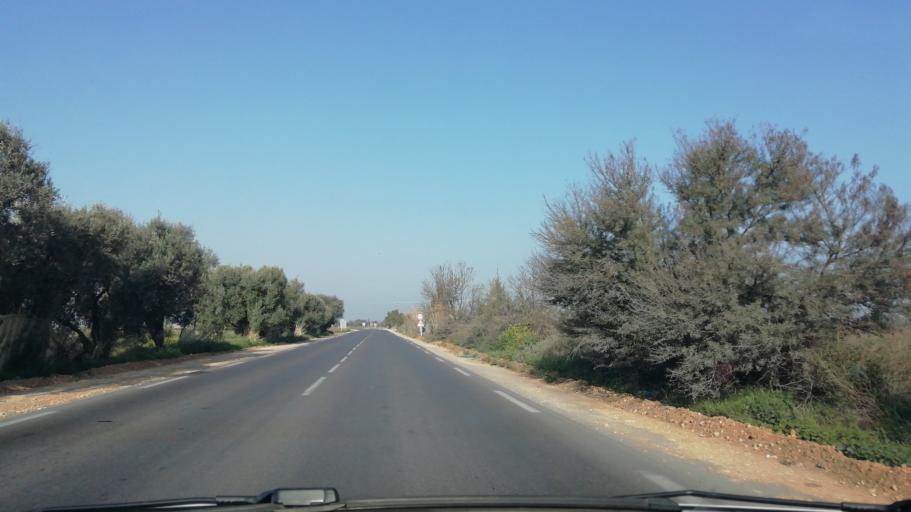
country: DZ
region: Mostaganem
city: Mostaganem
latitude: 35.7554
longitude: 0.1119
